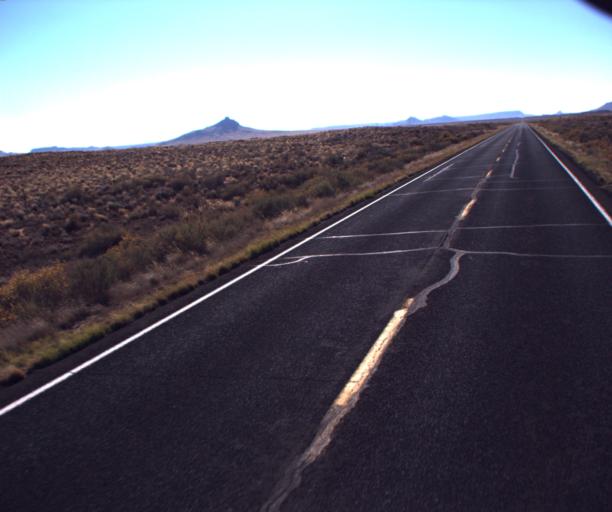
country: US
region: Arizona
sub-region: Navajo County
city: Dilkon
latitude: 35.5903
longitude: -110.4673
